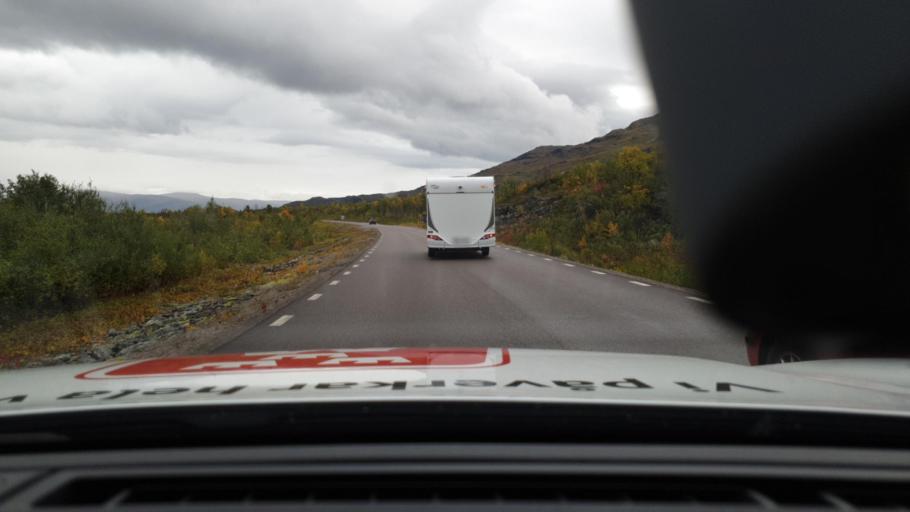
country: NO
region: Troms
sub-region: Bardu
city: Setermoen
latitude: 68.4297
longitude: 18.4705
